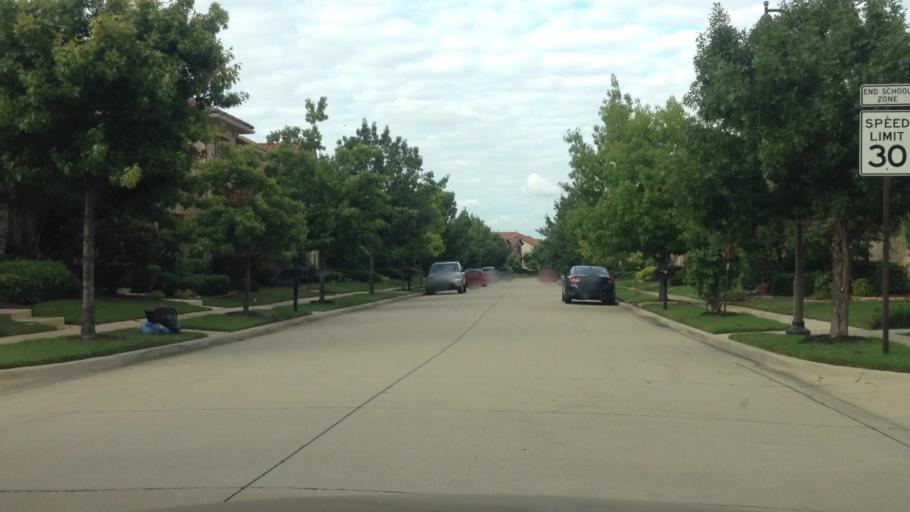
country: US
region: Texas
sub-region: Dallas County
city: Farmers Branch
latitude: 32.9046
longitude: -96.9367
